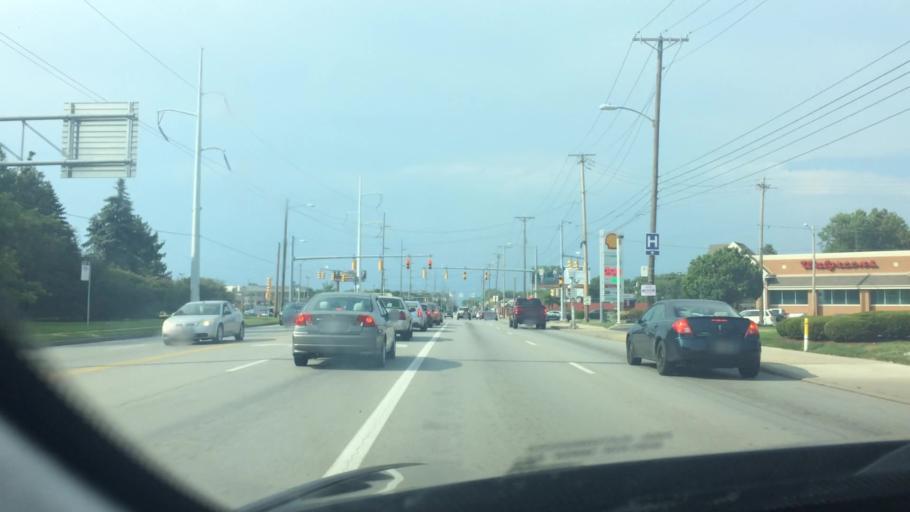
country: US
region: Ohio
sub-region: Lucas County
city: Ottawa Hills
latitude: 41.6887
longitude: -83.6231
